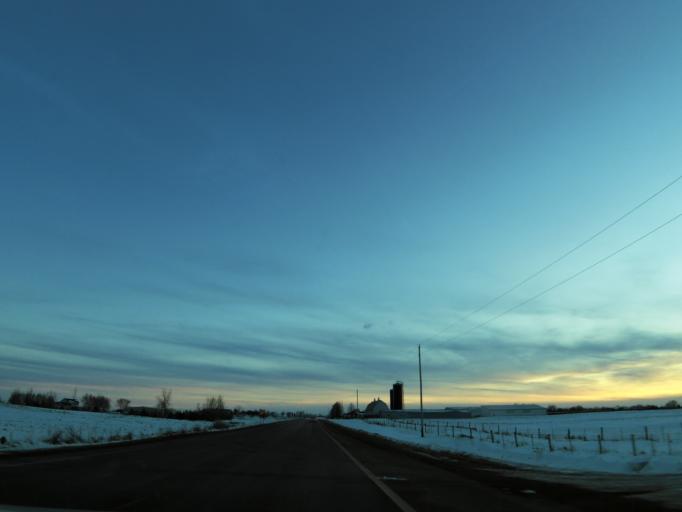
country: US
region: Minnesota
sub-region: Carver County
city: Chaska
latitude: 44.7451
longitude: -93.5618
